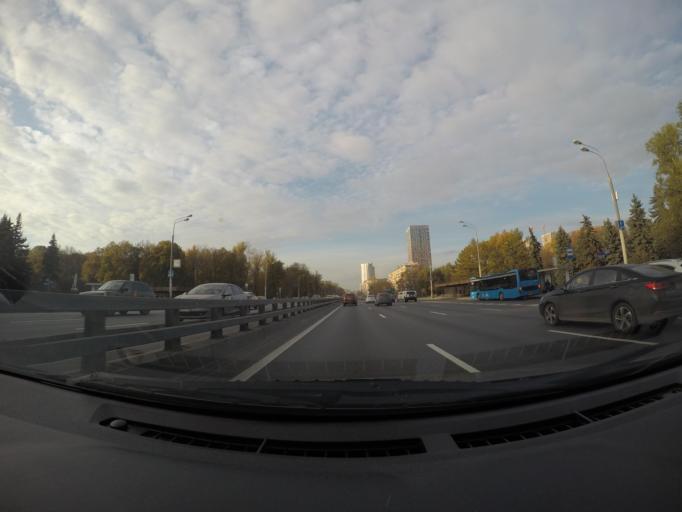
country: RU
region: Moskovskaya
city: Levoberezhnyy
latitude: 55.8518
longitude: 37.4727
